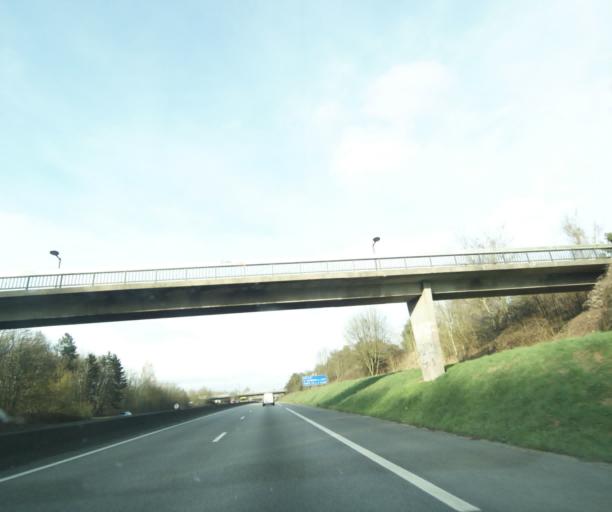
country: FR
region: Ile-de-France
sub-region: Departement des Yvelines
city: Bois-d'Arcy
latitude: 48.7897
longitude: 2.0381
